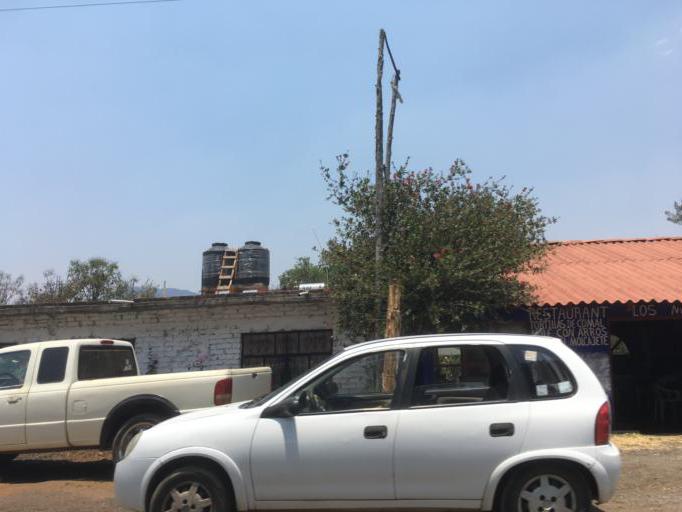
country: MX
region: Michoacan
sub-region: Morelia
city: Iratzio
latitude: 19.6316
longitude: -101.4680
